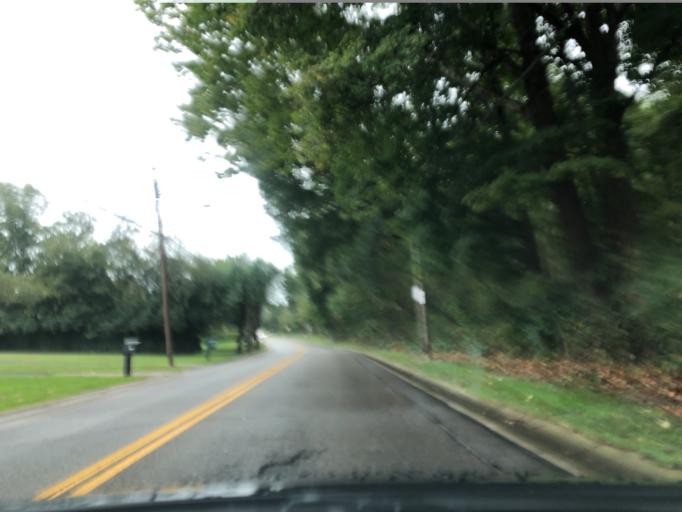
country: US
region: Ohio
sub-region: Hamilton County
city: Sharonville
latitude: 39.2829
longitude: -84.3995
